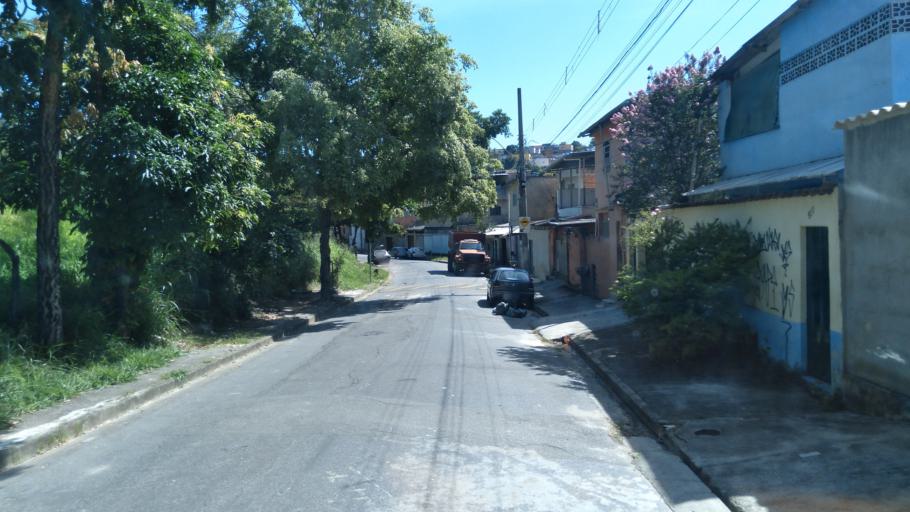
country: BR
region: Minas Gerais
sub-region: Belo Horizonte
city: Belo Horizonte
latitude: -19.8502
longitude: -43.9025
